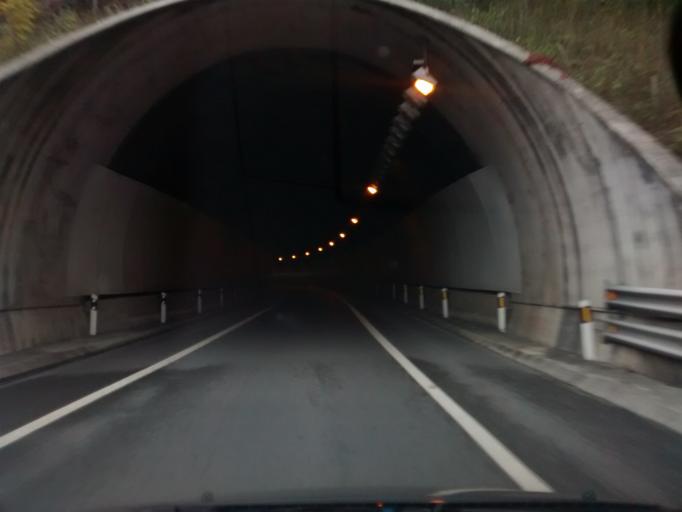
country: ES
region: Basque Country
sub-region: Provincia de Guipuzcoa
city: Elgoibar
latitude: 43.1927
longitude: -2.4335
